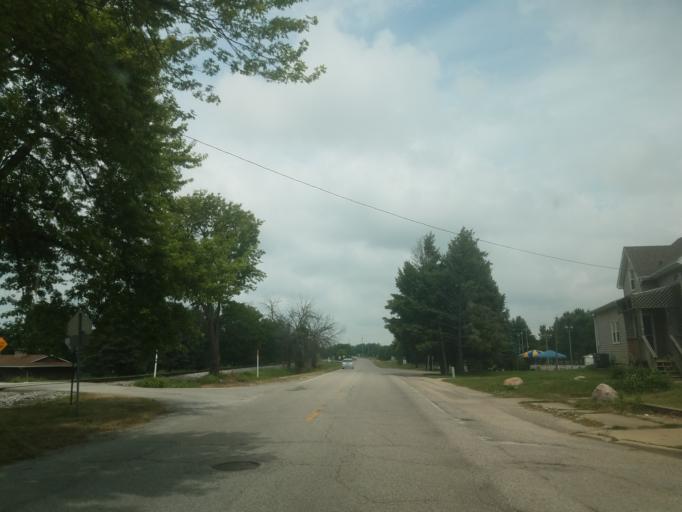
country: US
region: Illinois
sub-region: McLean County
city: Bloomington
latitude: 40.4845
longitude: -89.0146
